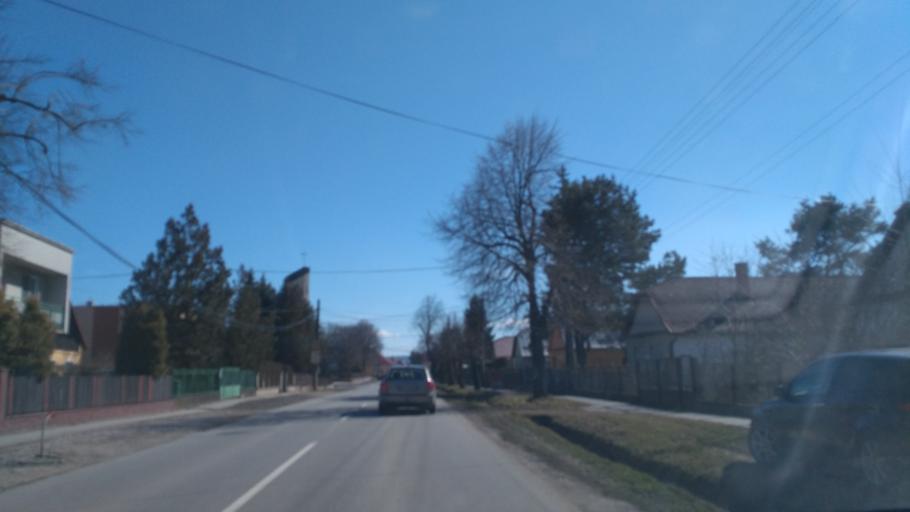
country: SK
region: Kosicky
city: Kosice
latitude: 48.6285
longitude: 21.3062
